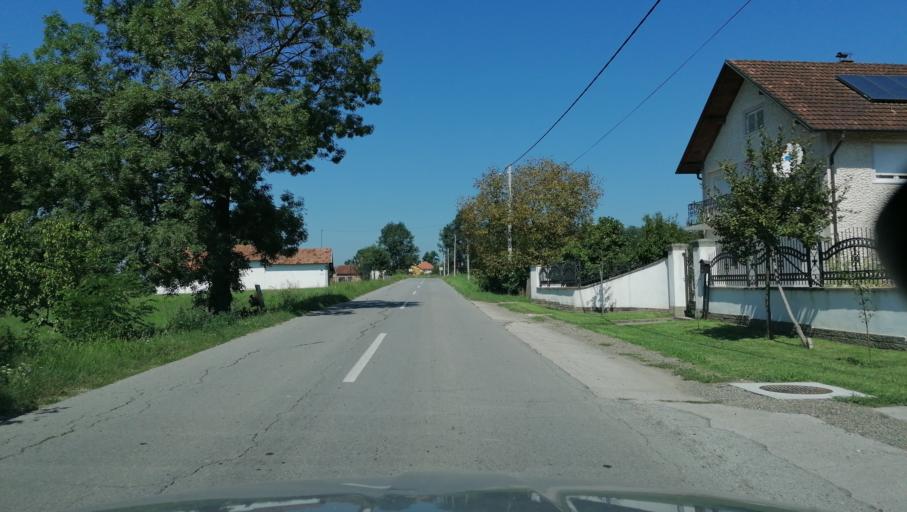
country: RS
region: Central Serbia
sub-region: Raski Okrug
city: Vrnjacka Banja
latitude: 43.6962
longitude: 20.8592
